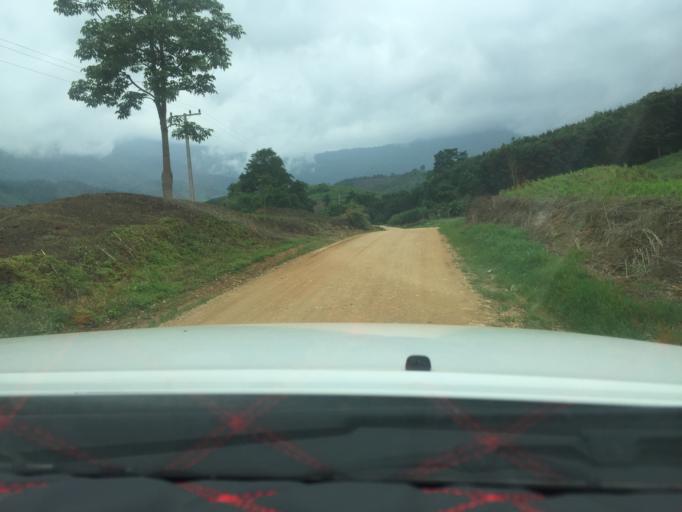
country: TH
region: Phayao
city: Phu Sang
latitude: 19.7425
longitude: 100.4573
